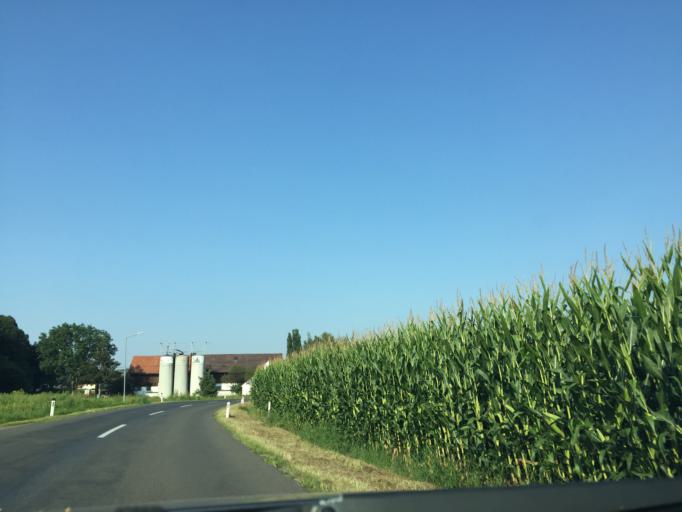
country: AT
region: Styria
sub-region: Politischer Bezirk Suedoststeiermark
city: Deutsch Goritz
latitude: 46.7612
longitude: 15.8441
